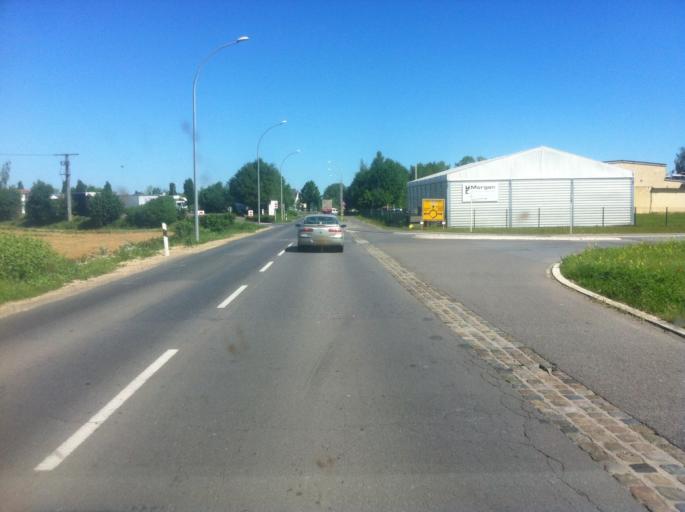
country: LU
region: Luxembourg
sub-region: Canton de Capellen
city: Koerich
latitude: 49.6449
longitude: 5.9559
